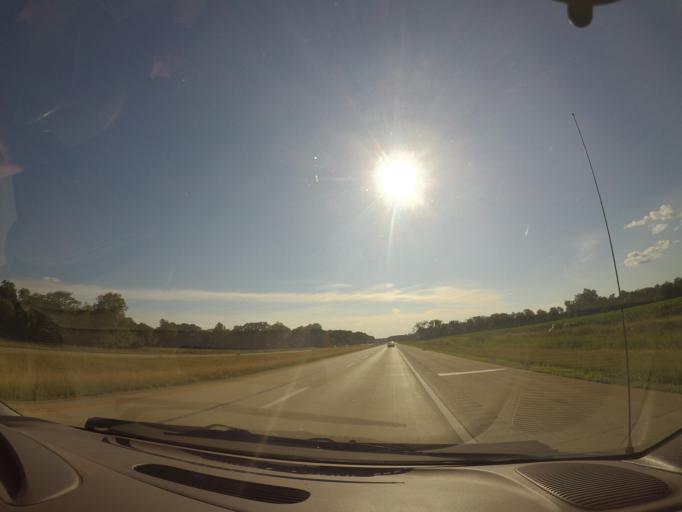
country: US
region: Ohio
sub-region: Henry County
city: Liberty Center
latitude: 41.4332
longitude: -83.9500
